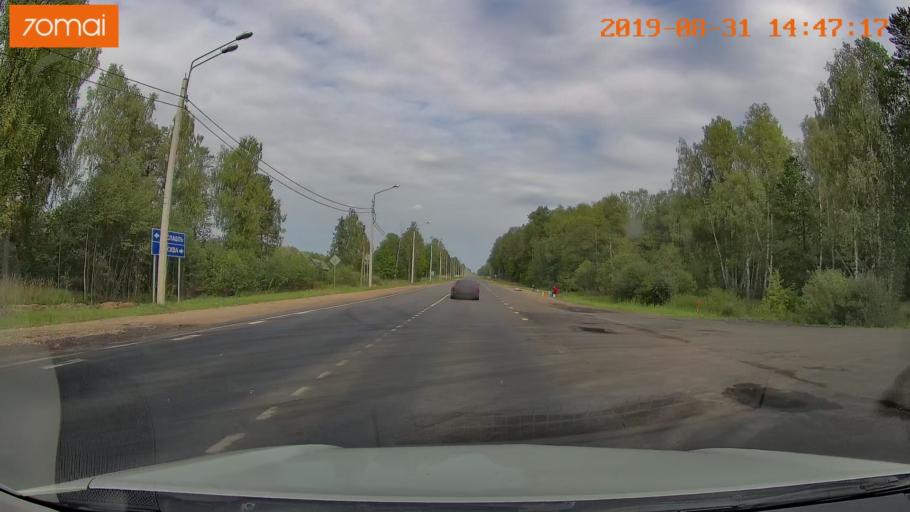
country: RU
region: Kaluga
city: Betlitsa
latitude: 54.2385
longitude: 33.7232
